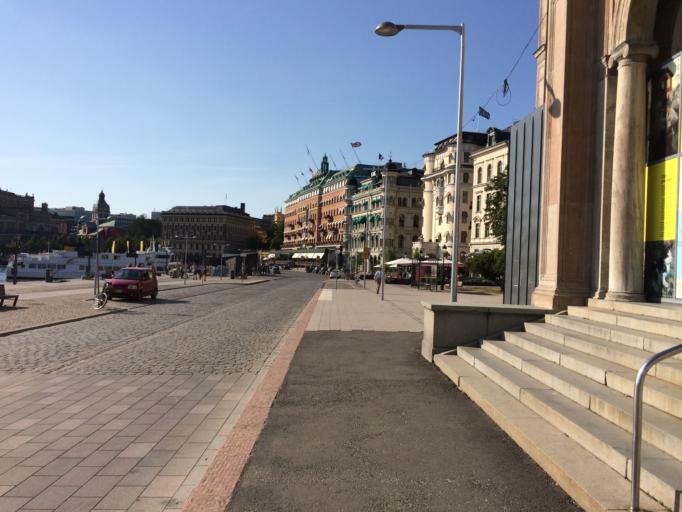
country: SE
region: Stockholm
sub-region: Stockholms Kommun
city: OEstermalm
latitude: 59.3283
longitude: 18.0777
